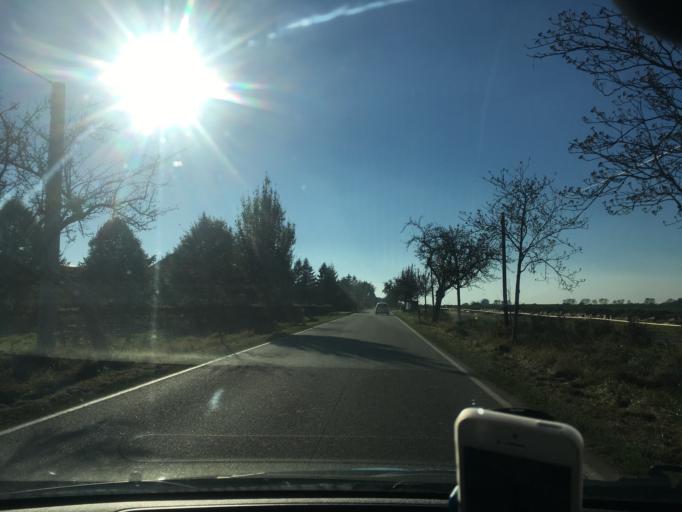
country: DE
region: Mecklenburg-Vorpommern
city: Wittenburg
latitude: 53.5405
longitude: 11.1358
